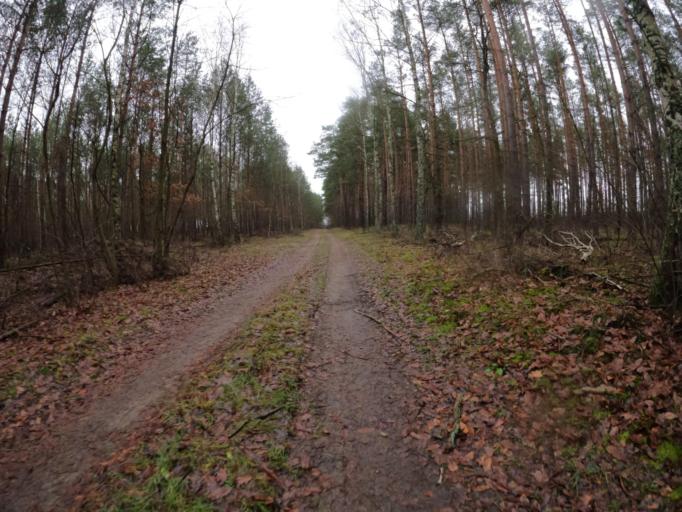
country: PL
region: West Pomeranian Voivodeship
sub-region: Powiat mysliborski
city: Debno
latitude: 52.7717
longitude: 14.7569
